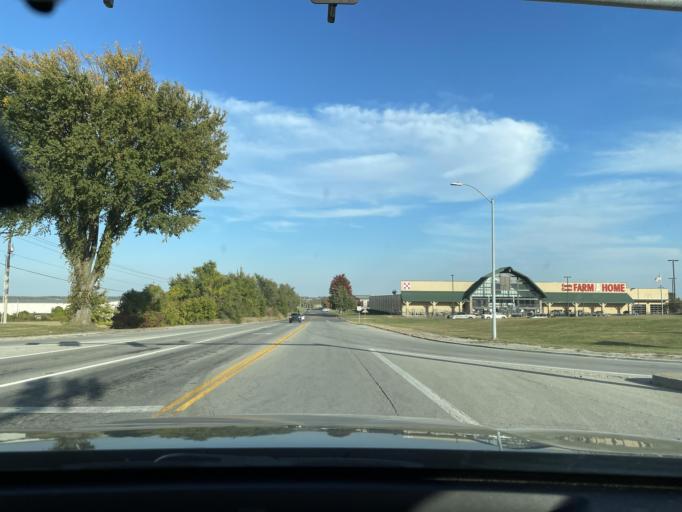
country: US
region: Missouri
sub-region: Buchanan County
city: Saint Joseph
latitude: 39.7554
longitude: -94.7680
